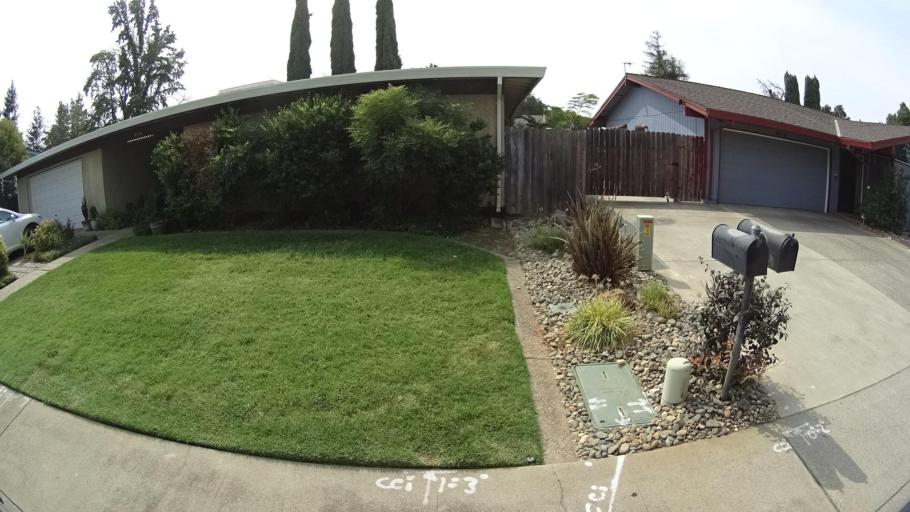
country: US
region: California
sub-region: Sacramento County
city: Elk Grove
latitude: 38.4128
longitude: -121.3797
